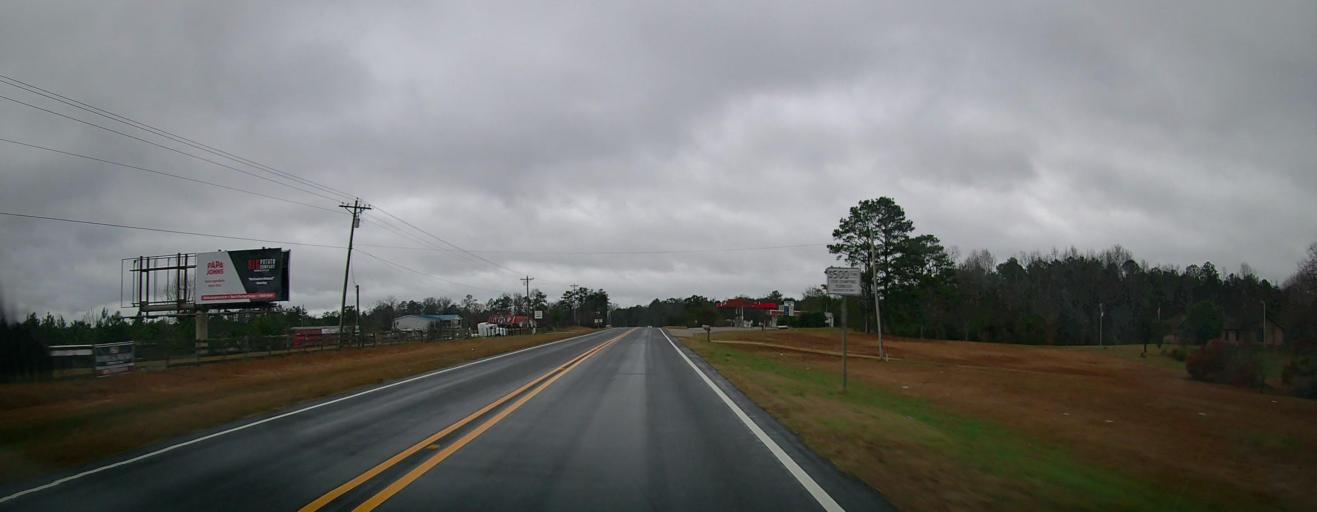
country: US
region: Alabama
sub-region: Chilton County
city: Thorsby
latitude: 32.7923
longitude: -86.9062
